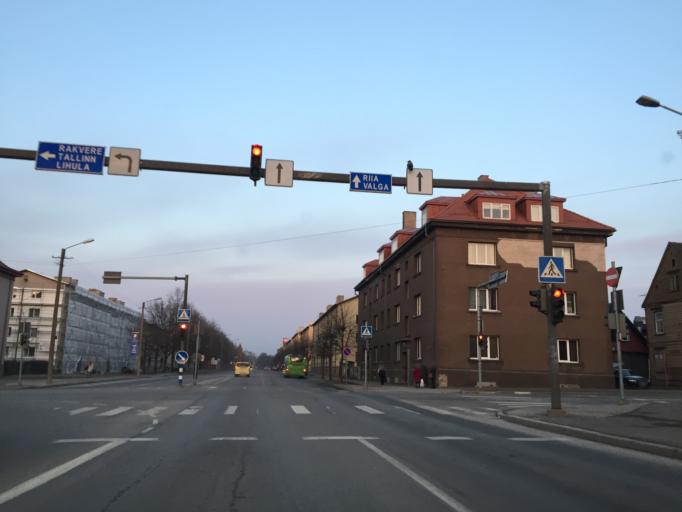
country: EE
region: Paernumaa
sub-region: Paernu linn
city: Parnu
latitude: 58.3858
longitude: 24.4968
